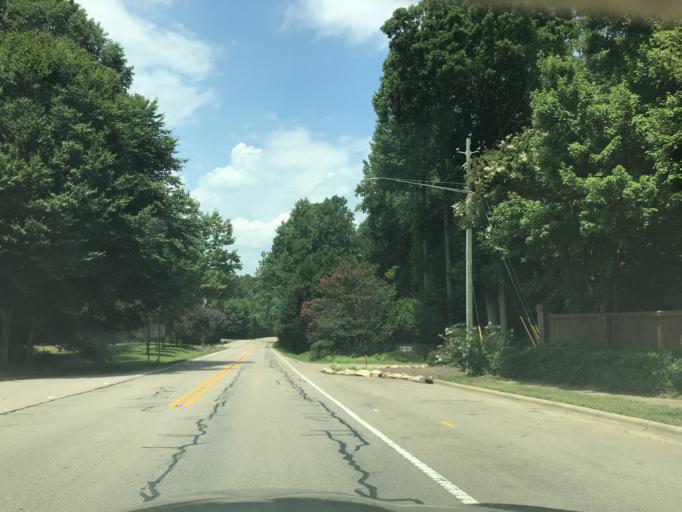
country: US
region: North Carolina
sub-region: Wake County
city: West Raleigh
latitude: 35.8278
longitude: -78.7127
